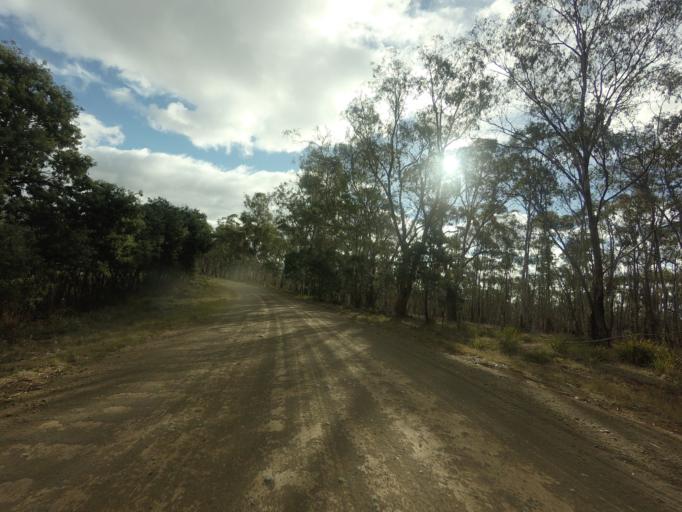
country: AU
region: Tasmania
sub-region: Brighton
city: Bridgewater
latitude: -42.4594
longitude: 147.2609
